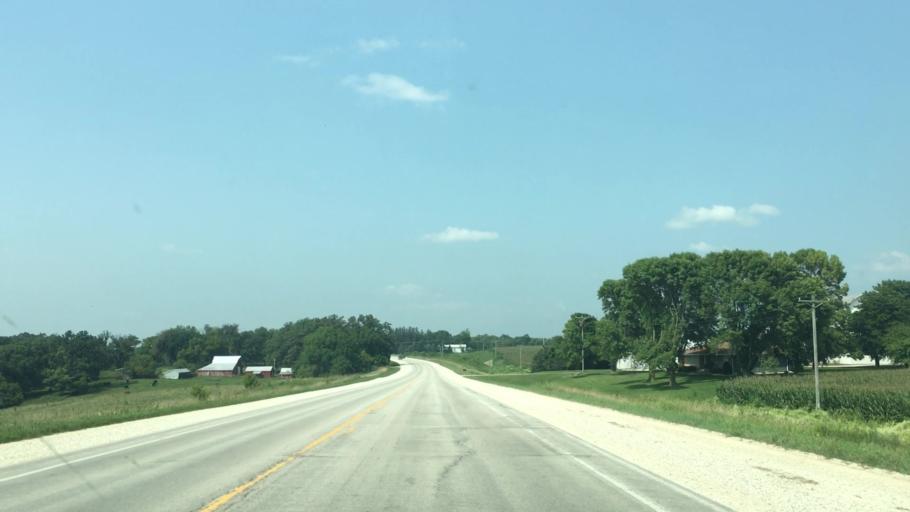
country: US
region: Iowa
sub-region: Winneshiek County
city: Decorah
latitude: 43.4233
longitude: -91.8591
